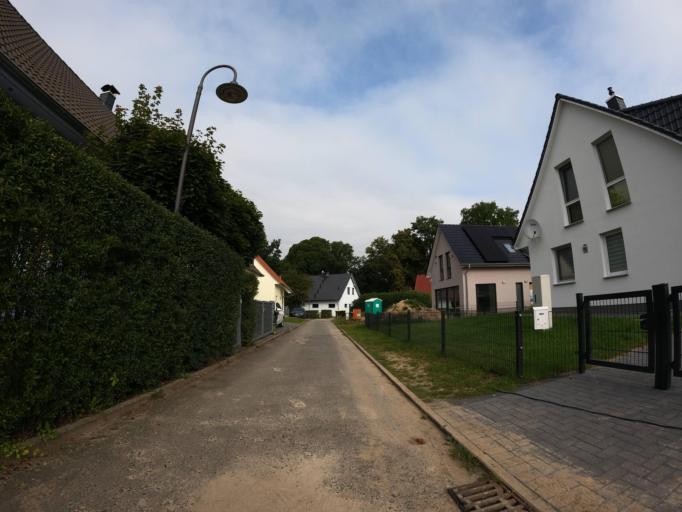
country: DE
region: Mecklenburg-Vorpommern
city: Malchow
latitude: 53.4903
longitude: 12.4837
